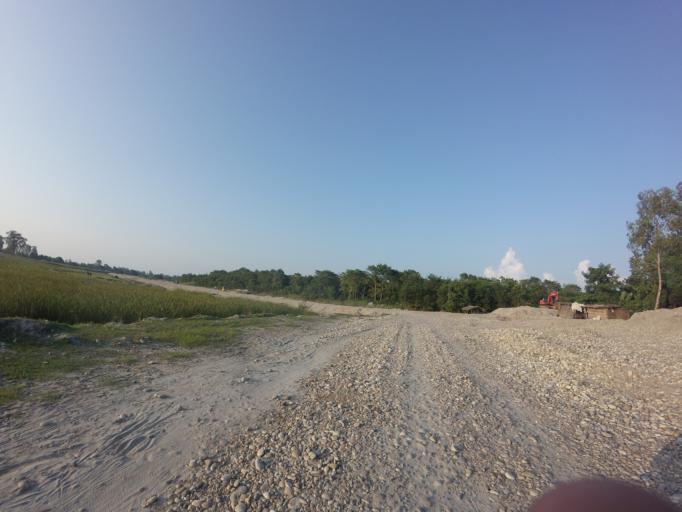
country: NP
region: Far Western
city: Tikapur
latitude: 28.4463
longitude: 81.0749
